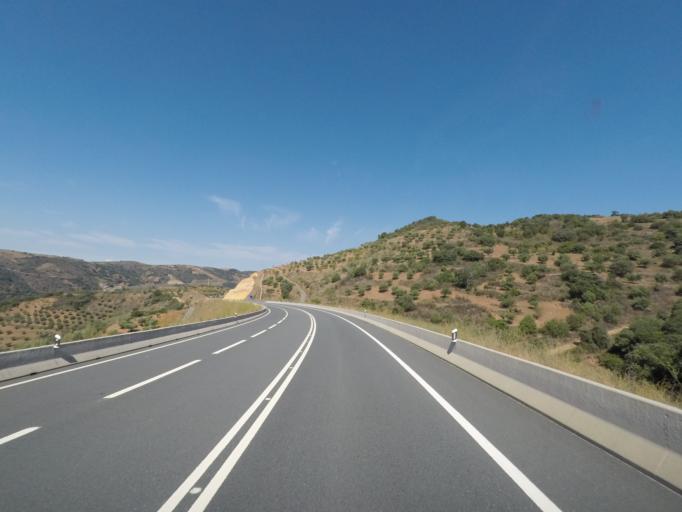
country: PT
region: Braganca
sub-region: Alfandega da Fe
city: Alfandega da Fe
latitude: 41.3028
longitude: -6.9006
